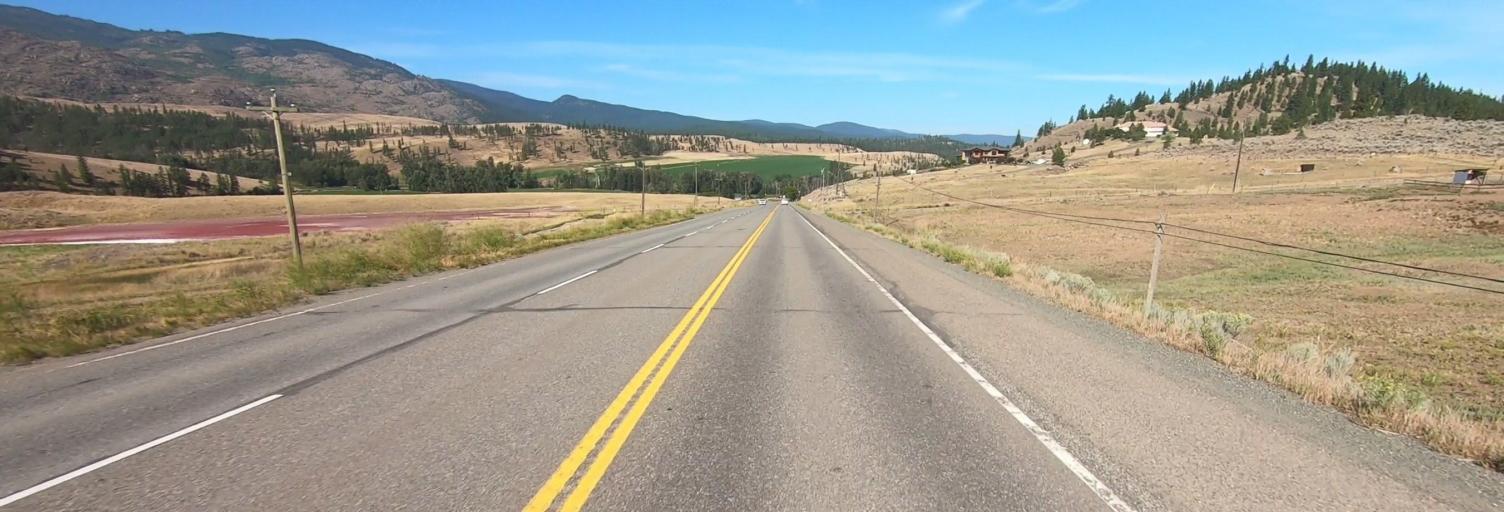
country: CA
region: British Columbia
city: Kamloops
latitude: 50.6617
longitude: -120.5454
